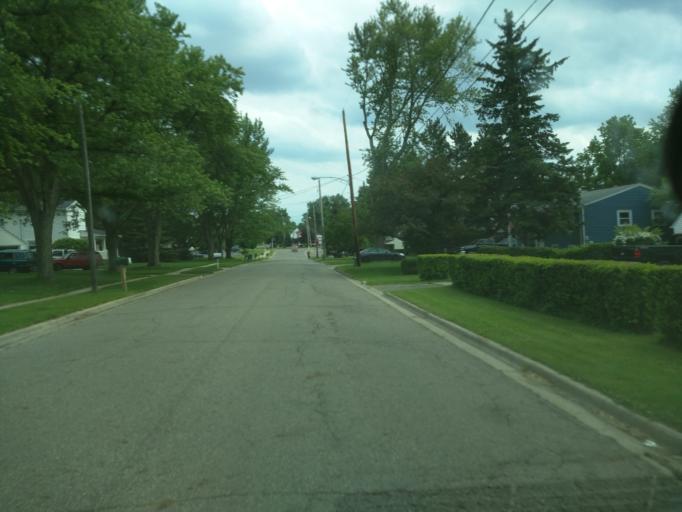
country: US
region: Michigan
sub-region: Eaton County
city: Waverly
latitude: 42.7430
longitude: -84.6135
